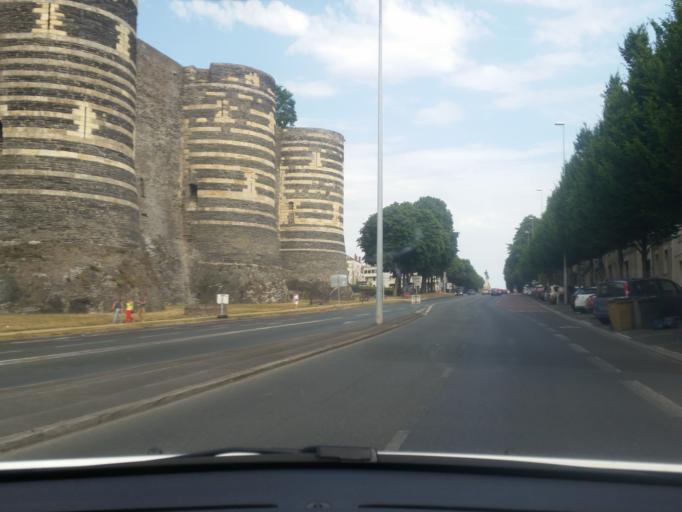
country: FR
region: Pays de la Loire
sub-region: Departement de Maine-et-Loire
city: Angers
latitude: 47.4697
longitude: -0.5616
